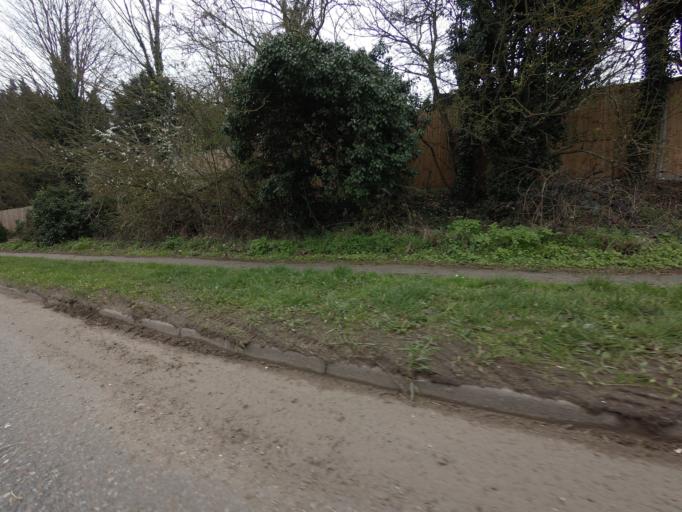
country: GB
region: England
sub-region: Greater London
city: Bexley
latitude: 51.4132
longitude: 0.1357
